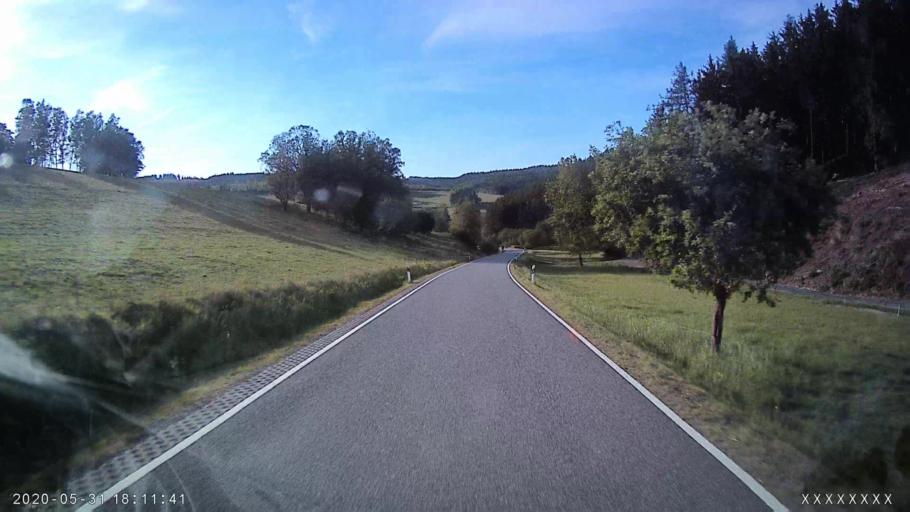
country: DE
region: Hesse
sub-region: Regierungsbezirk Giessen
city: Haiger
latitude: 50.8245
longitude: 8.2448
